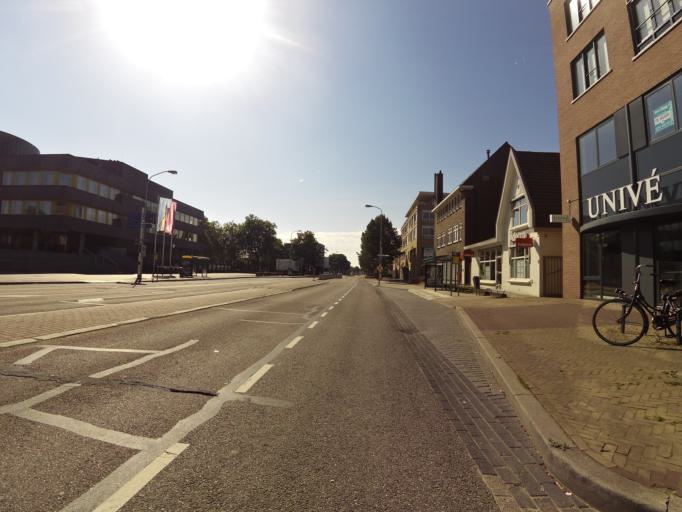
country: NL
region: Gelderland
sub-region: Gemeente Doetinchem
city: Doetinchem
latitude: 51.9632
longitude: 6.2914
